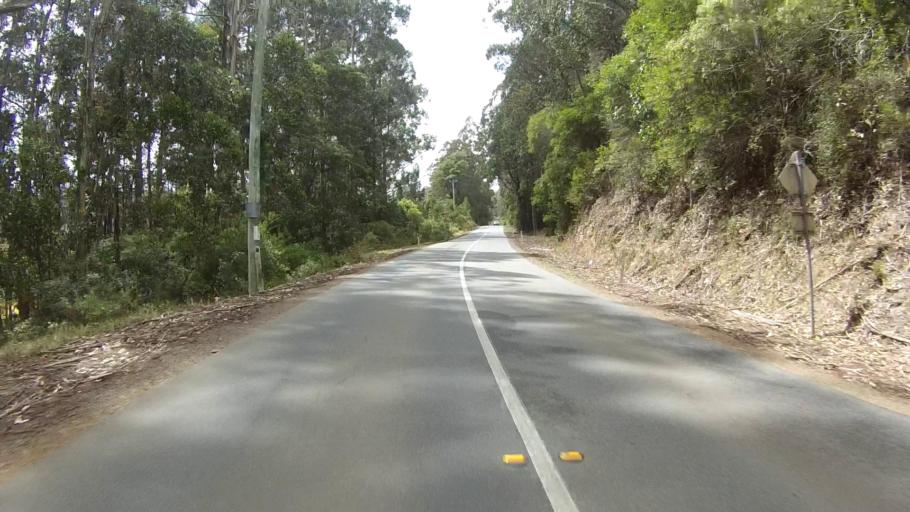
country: AU
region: Tasmania
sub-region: Kingborough
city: Kettering
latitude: -43.1298
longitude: 147.1595
